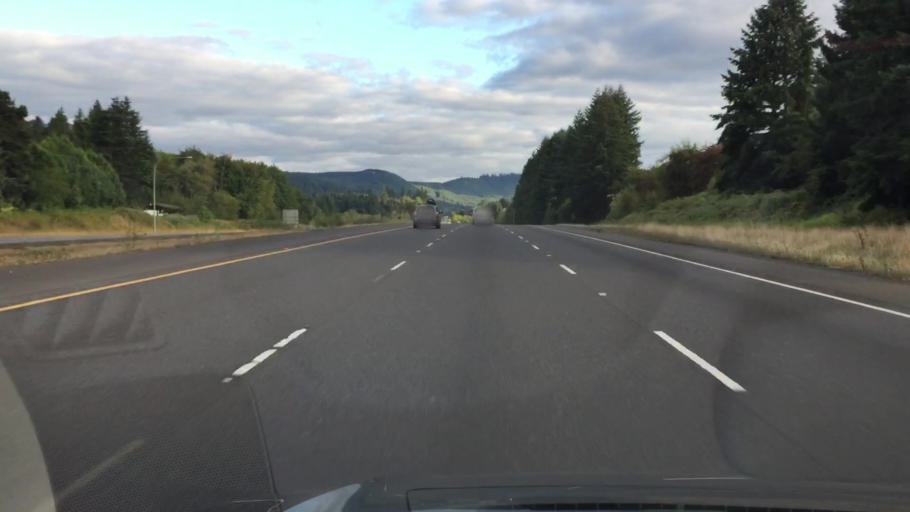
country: US
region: Washington
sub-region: Cowlitz County
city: Castle Rock
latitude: 46.2823
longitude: -122.9017
